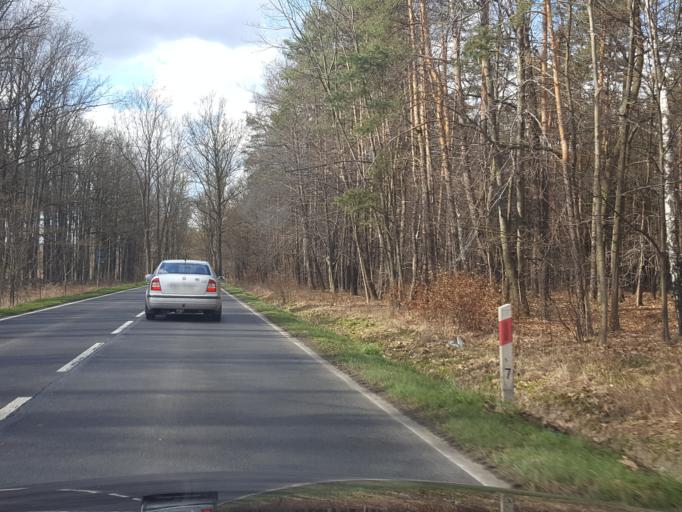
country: PL
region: Silesian Voivodeship
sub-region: Powiat pszczynski
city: Kobior
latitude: 50.0683
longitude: 18.9145
